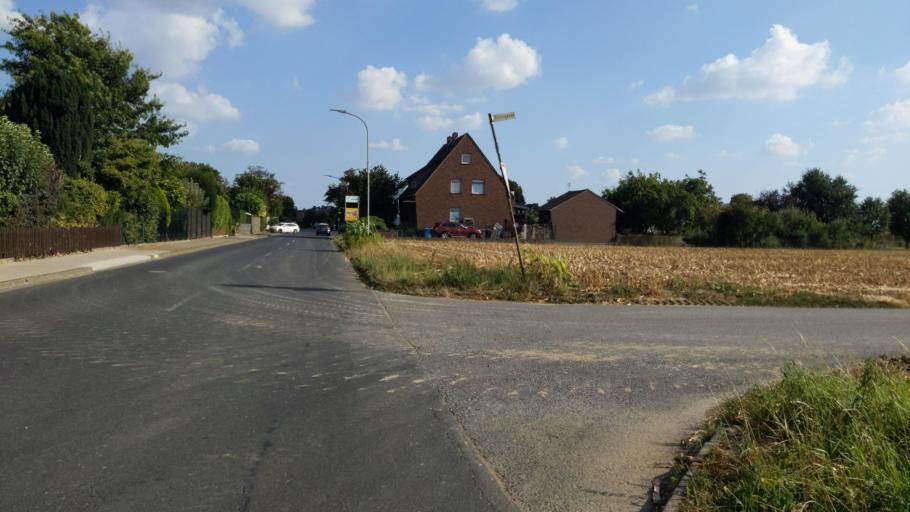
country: DE
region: North Rhine-Westphalia
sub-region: Regierungsbezirk Dusseldorf
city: Kaarst
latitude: 51.2186
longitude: 6.5713
